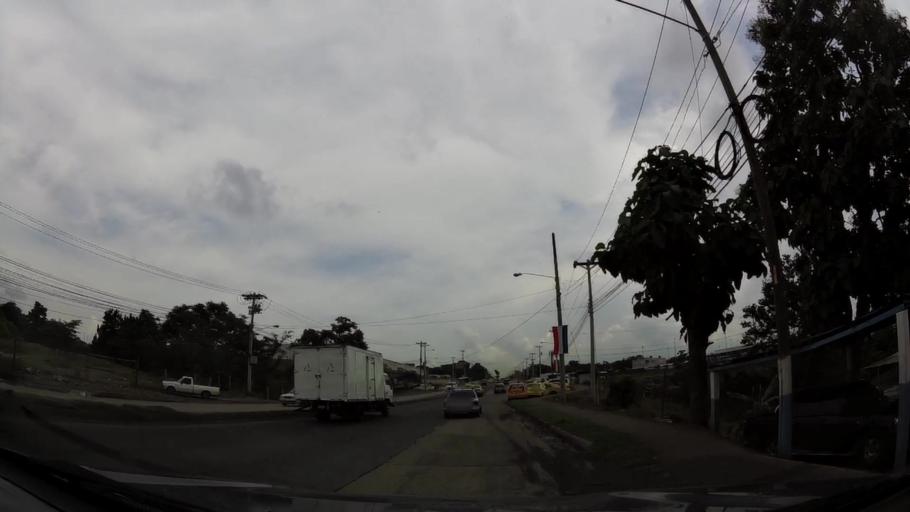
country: PA
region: Panama
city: Cabra Numero Uno
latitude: 9.1025
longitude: -79.3593
